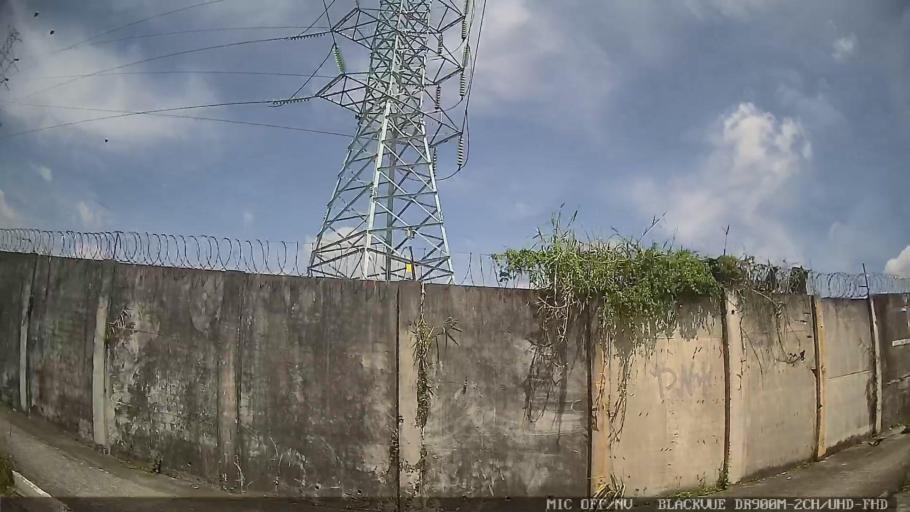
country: BR
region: Sao Paulo
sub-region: Poa
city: Poa
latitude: -23.5272
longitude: -46.3258
